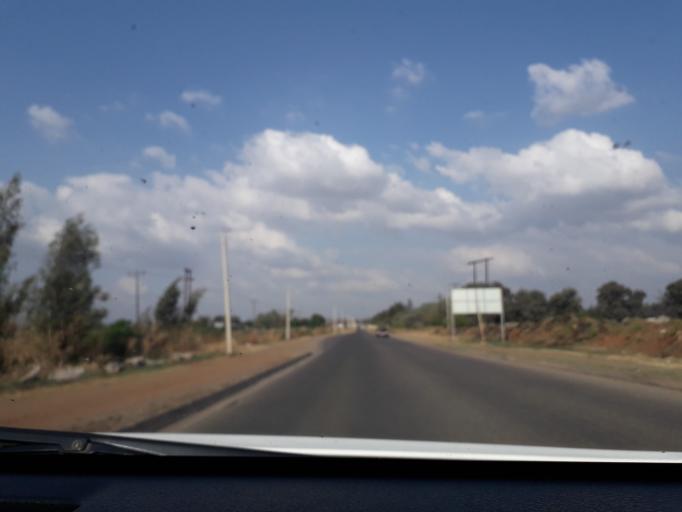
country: ZA
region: Gauteng
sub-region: Ekurhuleni Metropolitan Municipality
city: Tembisa
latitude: -25.9413
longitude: 28.2356
